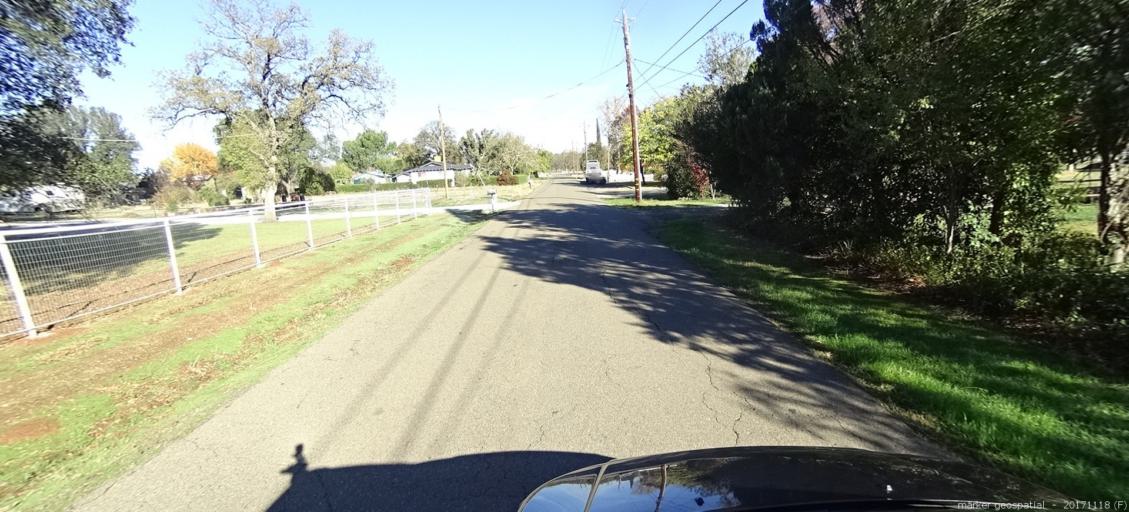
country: US
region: California
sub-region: Shasta County
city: Cottonwood
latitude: 40.3868
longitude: -122.3215
